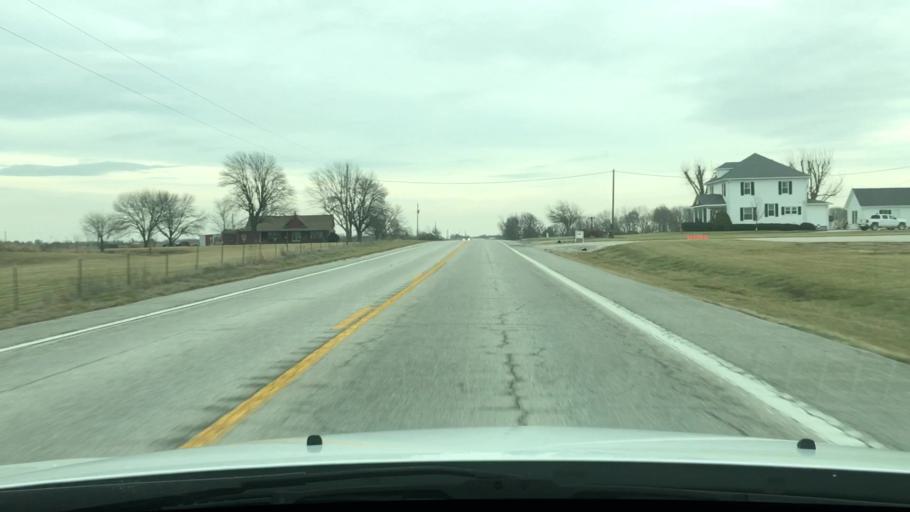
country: US
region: Missouri
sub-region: Audrain County
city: Vandalia
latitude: 39.2804
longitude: -91.6193
